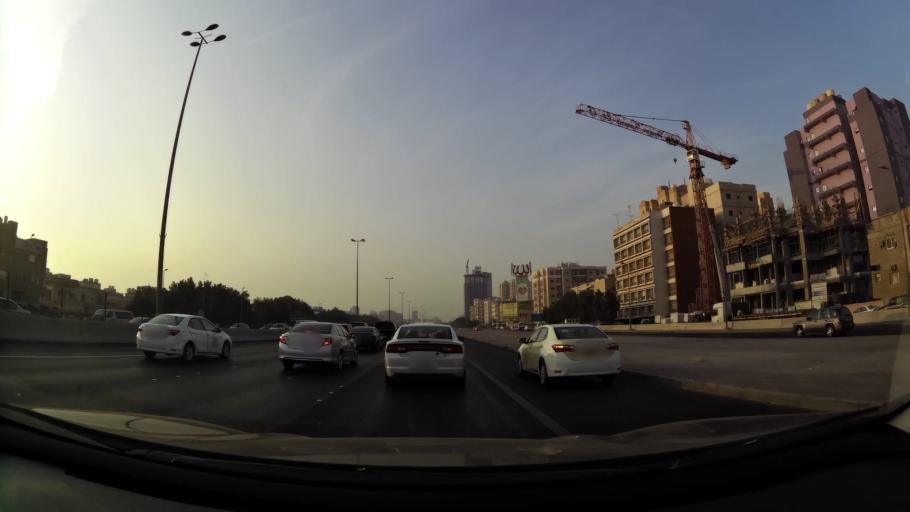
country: KW
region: Muhafazat Hawalli
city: Hawalli
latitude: 29.3238
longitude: 48.0454
